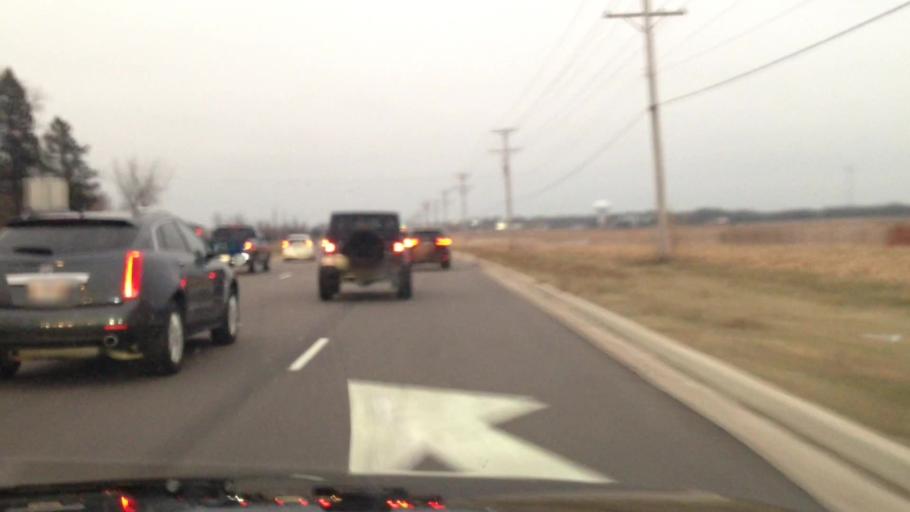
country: US
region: Illinois
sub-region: McHenry County
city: Lake in the Hills
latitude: 42.1392
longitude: -88.3360
